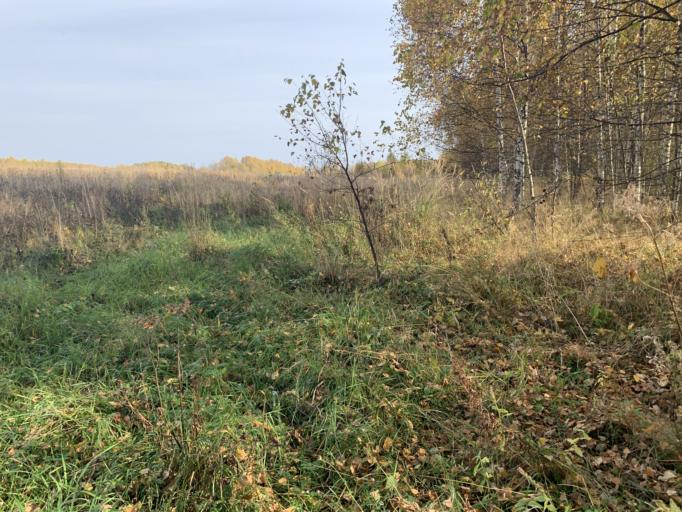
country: RU
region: Jaroslavl
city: Porech'ye-Rybnoye
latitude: 57.0031
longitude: 39.4001
